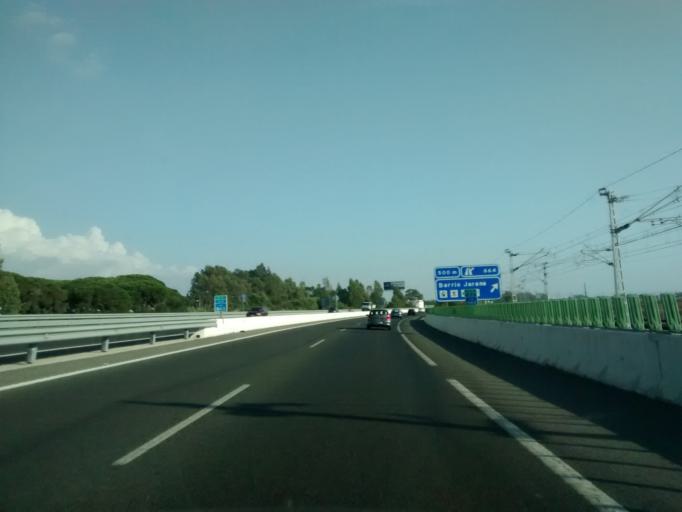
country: ES
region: Andalusia
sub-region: Provincia de Cadiz
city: Puerto Real
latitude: 36.5057
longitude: -6.1458
